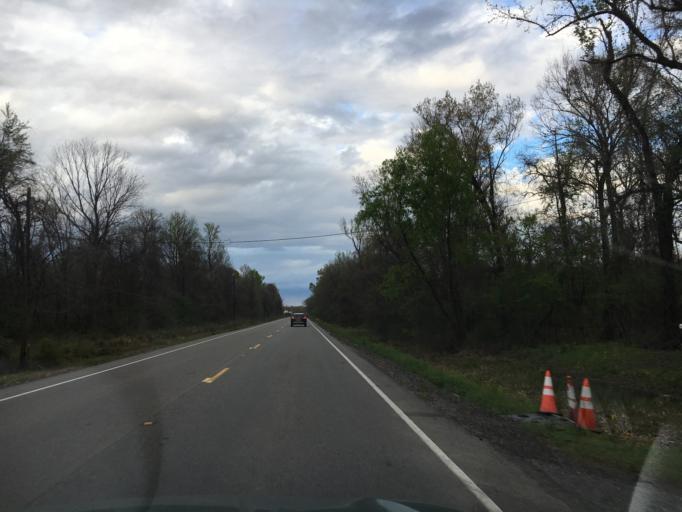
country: US
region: Louisiana
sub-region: West Baton Rouge Parish
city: Erwinville
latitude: 30.4725
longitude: -91.3980
